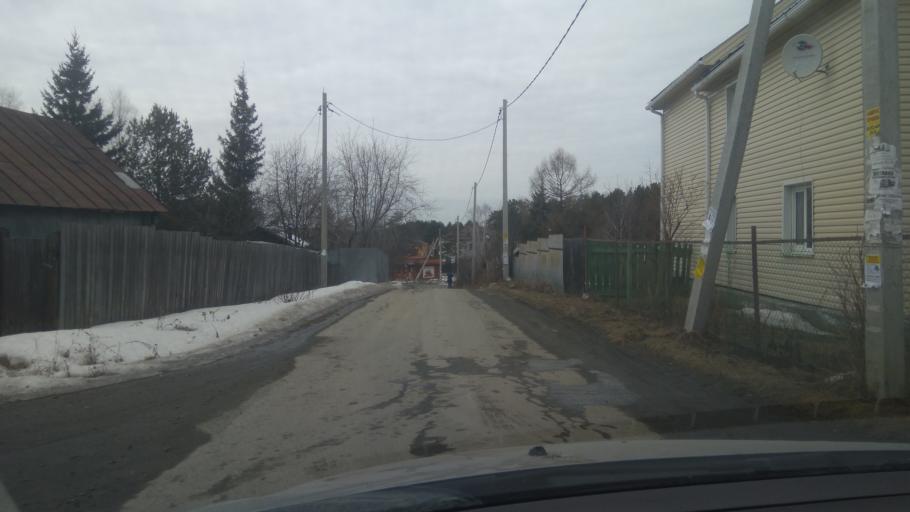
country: RU
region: Sverdlovsk
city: Severka
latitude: 56.8519
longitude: 60.3850
